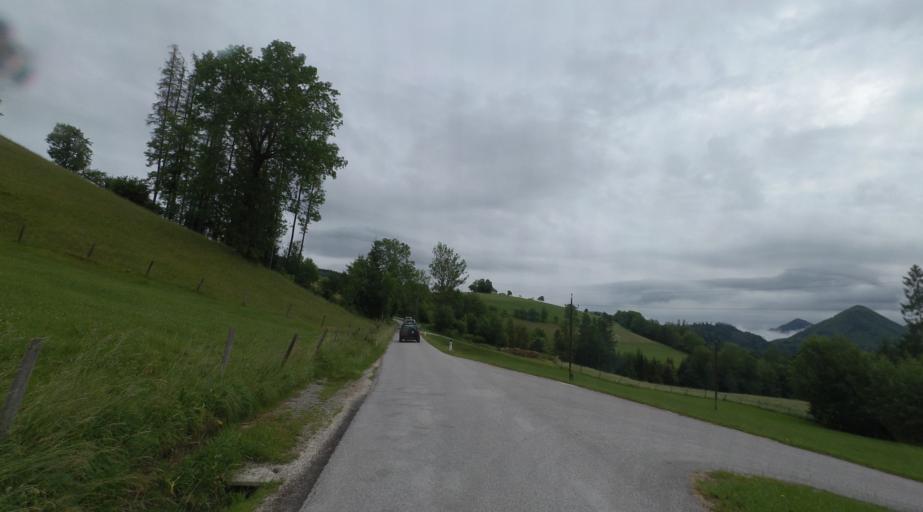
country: AT
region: Upper Austria
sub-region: Politischer Bezirk Kirchdorf an der Krems
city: Micheldorf in Oberoesterreich
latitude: 47.8958
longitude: 14.1591
